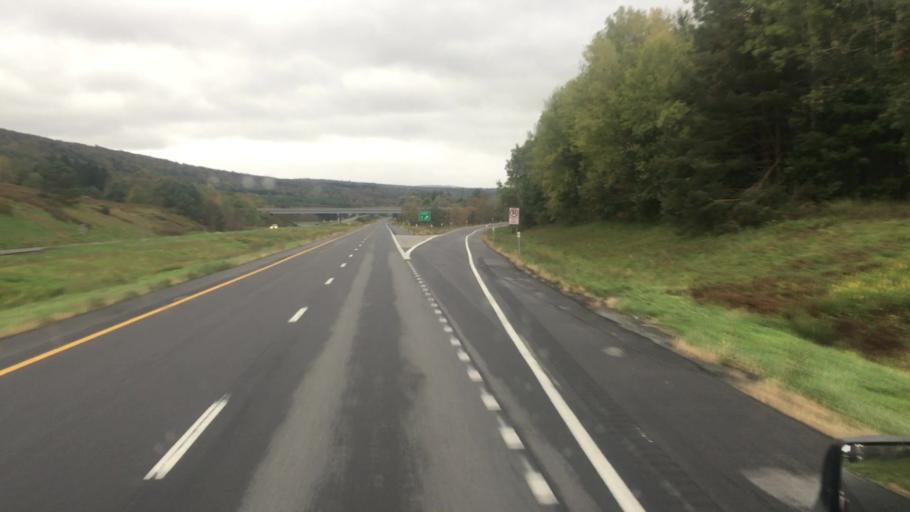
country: US
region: New York
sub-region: Chenango County
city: Bainbridge
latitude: 42.2272
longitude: -75.5117
